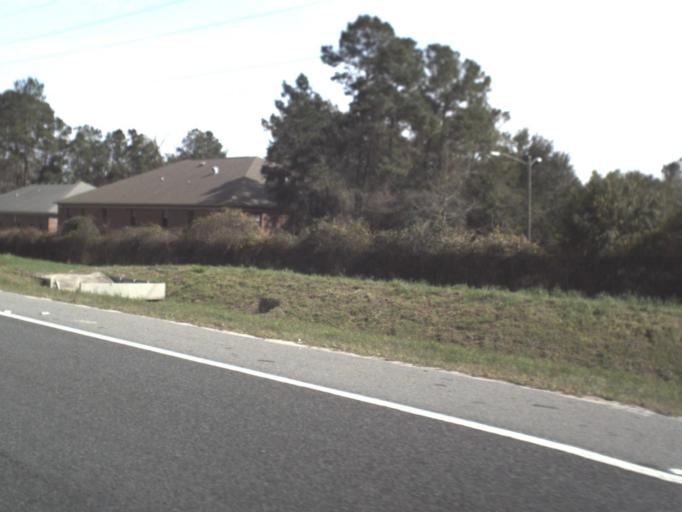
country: US
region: Florida
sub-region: Leon County
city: Tallahassee
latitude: 30.4782
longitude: -84.3552
